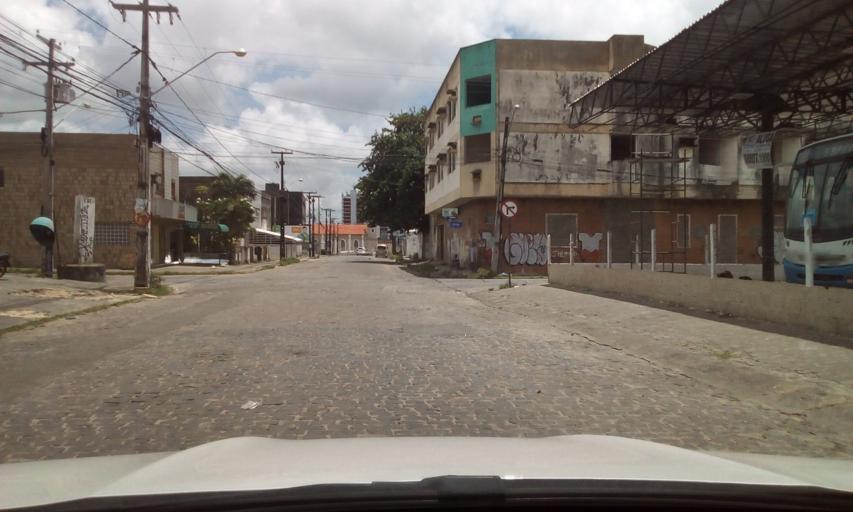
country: BR
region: Paraiba
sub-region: Joao Pessoa
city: Joao Pessoa
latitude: -7.1244
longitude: -34.8855
